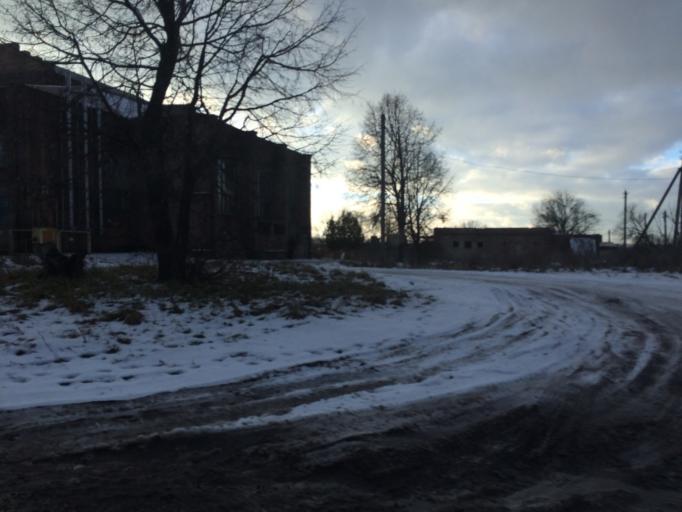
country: RU
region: Tula
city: Cherepet'
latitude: 54.1098
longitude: 36.3278
